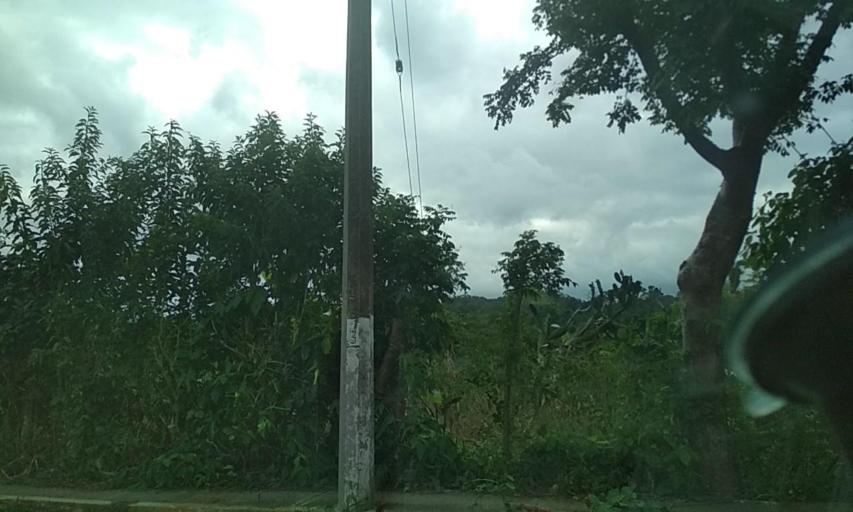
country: MX
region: Veracruz
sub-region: Papantla
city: Polutla
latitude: 20.5389
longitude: -97.2478
